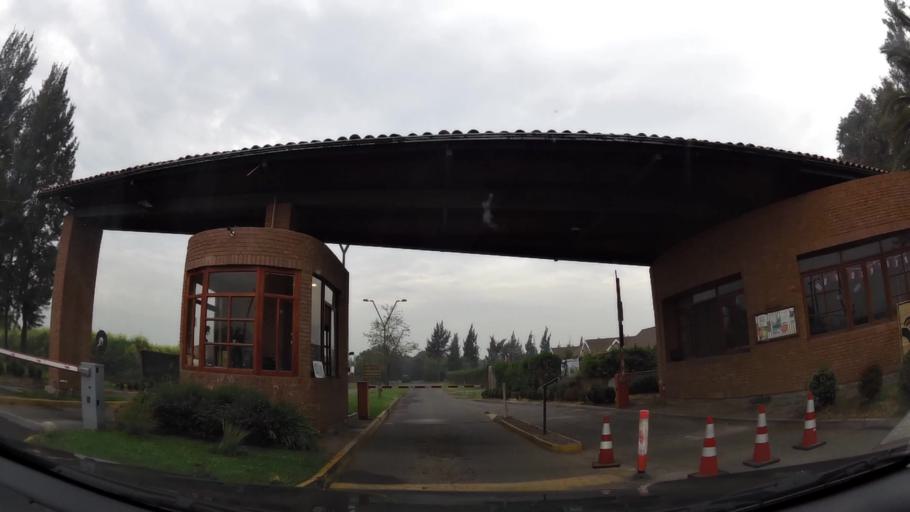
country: CL
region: Santiago Metropolitan
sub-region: Provincia de Chacabuco
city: Lampa
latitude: -33.2635
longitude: -70.7693
